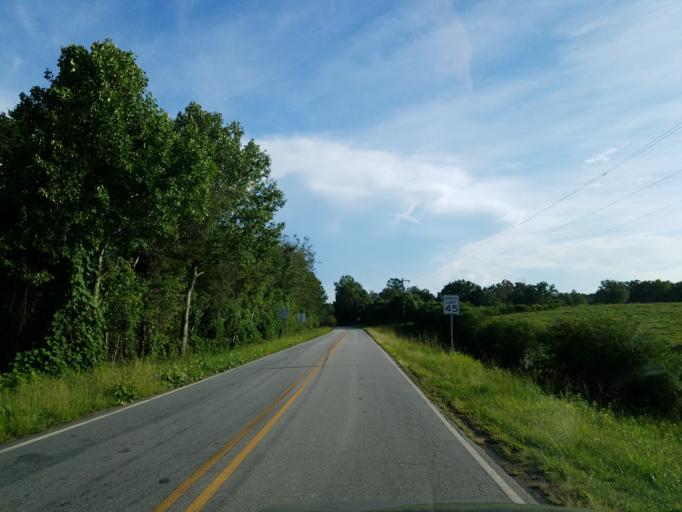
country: US
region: Georgia
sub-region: White County
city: Cleveland
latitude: 34.6069
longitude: -83.8597
